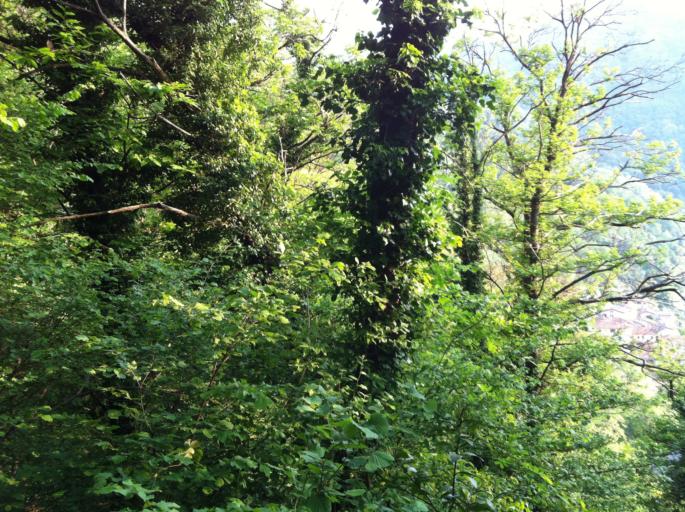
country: IT
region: Lombardy
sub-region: Provincia di Como
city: Menaggio
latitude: 46.0314
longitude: 9.2356
